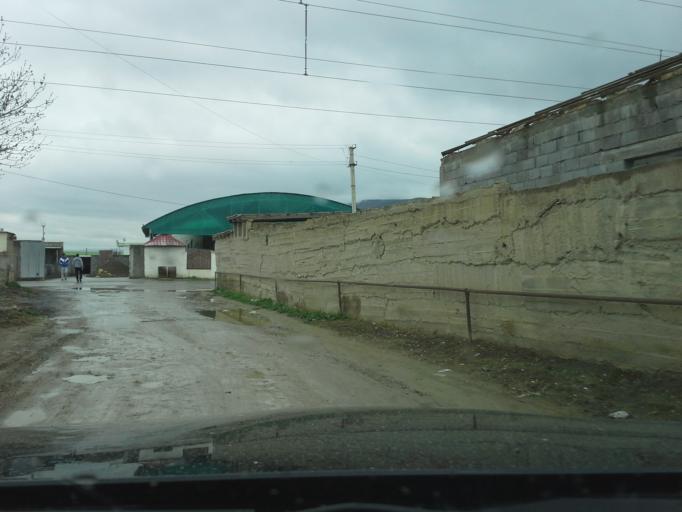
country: TM
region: Ahal
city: Abadan
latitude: 37.9512
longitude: 58.2060
